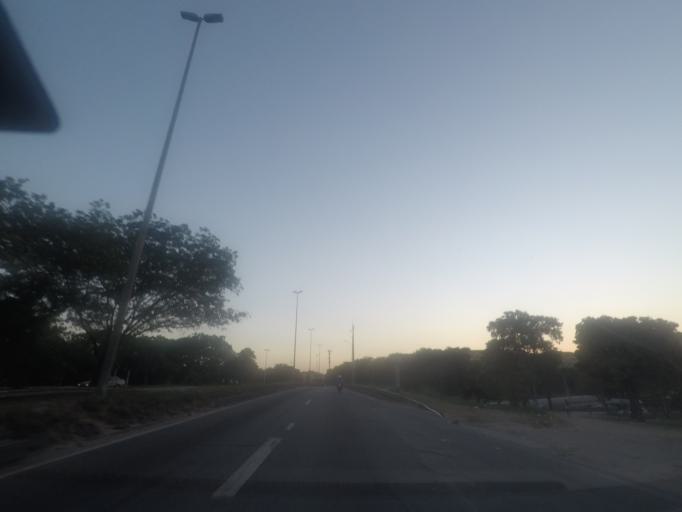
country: BR
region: Rio de Janeiro
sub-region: Duque De Caxias
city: Duque de Caxias
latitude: -22.8148
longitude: -43.2883
